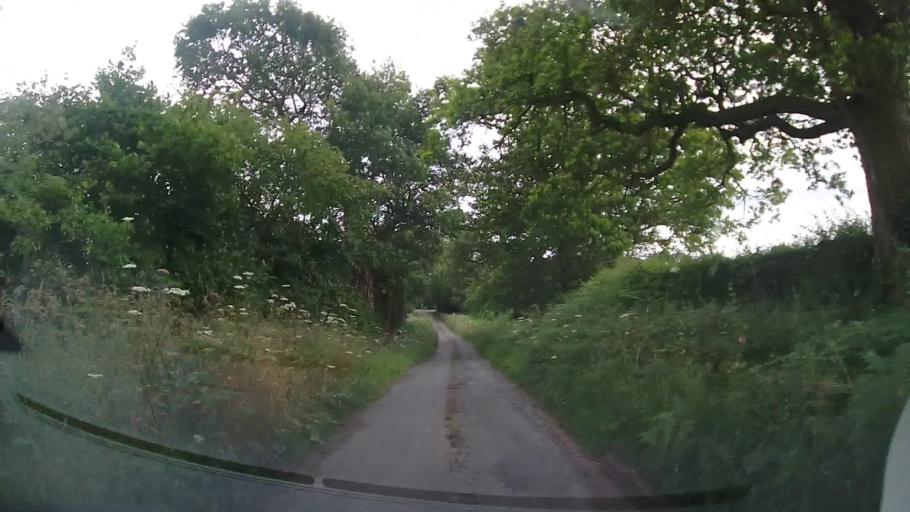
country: GB
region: England
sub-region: Shropshire
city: Whitchurch
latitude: 52.9360
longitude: -2.7285
